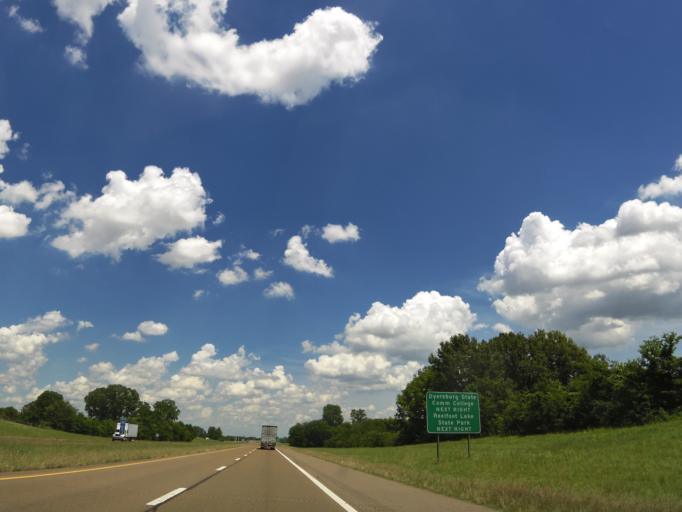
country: US
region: Tennessee
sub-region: Dyer County
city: Dyersburg
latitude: 36.0689
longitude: -89.4106
